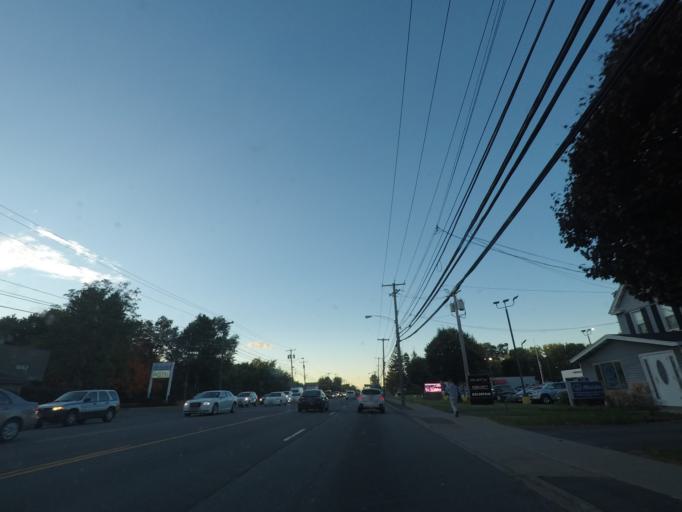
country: US
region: New York
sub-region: Albany County
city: Colonie
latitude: 42.7215
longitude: -73.8373
